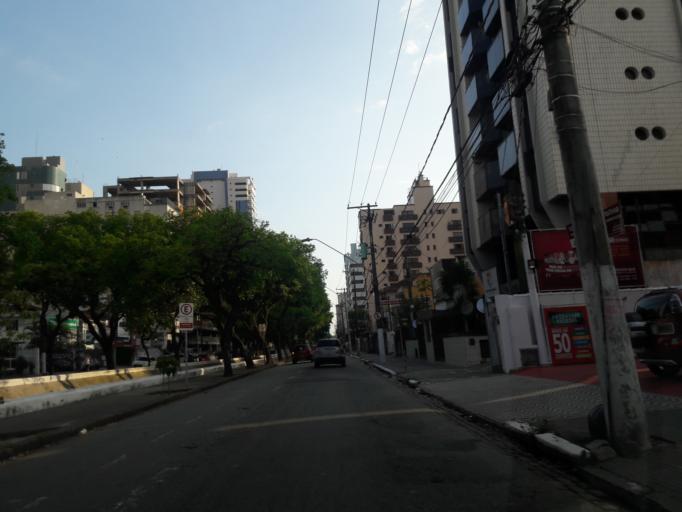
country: BR
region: Sao Paulo
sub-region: Santos
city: Santos
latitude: -23.9623
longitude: -46.3386
